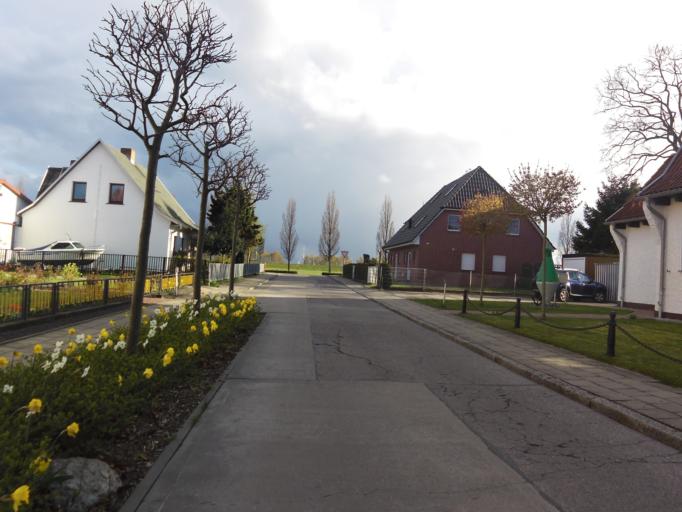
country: DE
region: Mecklenburg-Vorpommern
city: Zingst
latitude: 54.4346
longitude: 12.6928
